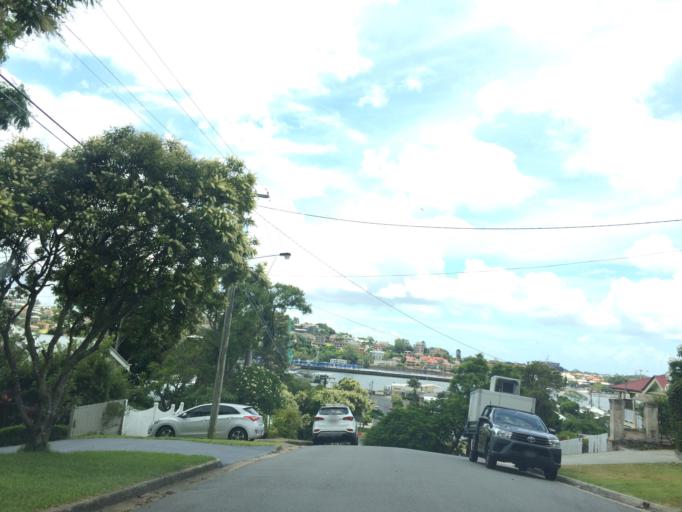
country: AU
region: Queensland
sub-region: Brisbane
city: Balmoral
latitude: -27.4460
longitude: 153.0596
